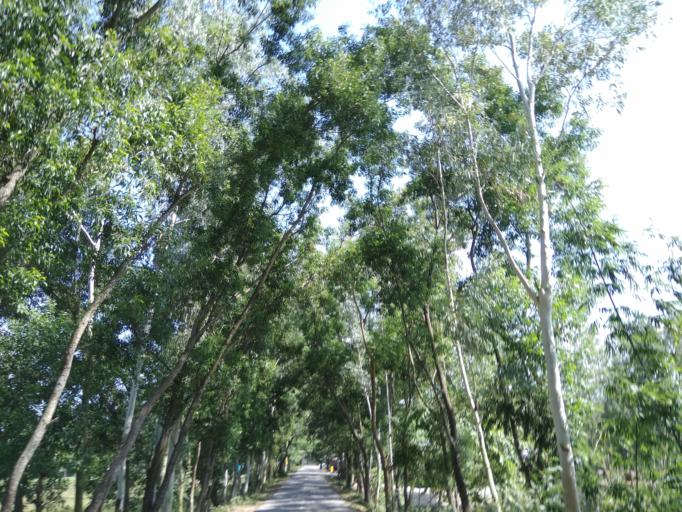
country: IN
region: West Bengal
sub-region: Koch Bihar
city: Haldibari
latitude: 26.1930
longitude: 88.6908
